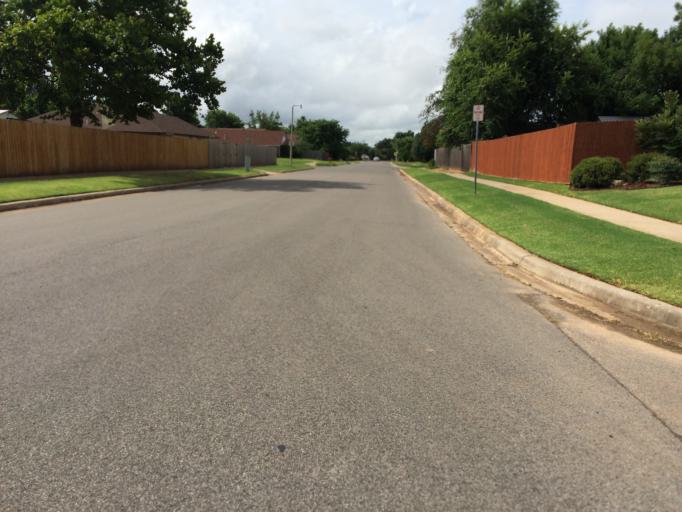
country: US
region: Oklahoma
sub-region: Cleveland County
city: Hall Park
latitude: 35.2213
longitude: -97.4134
